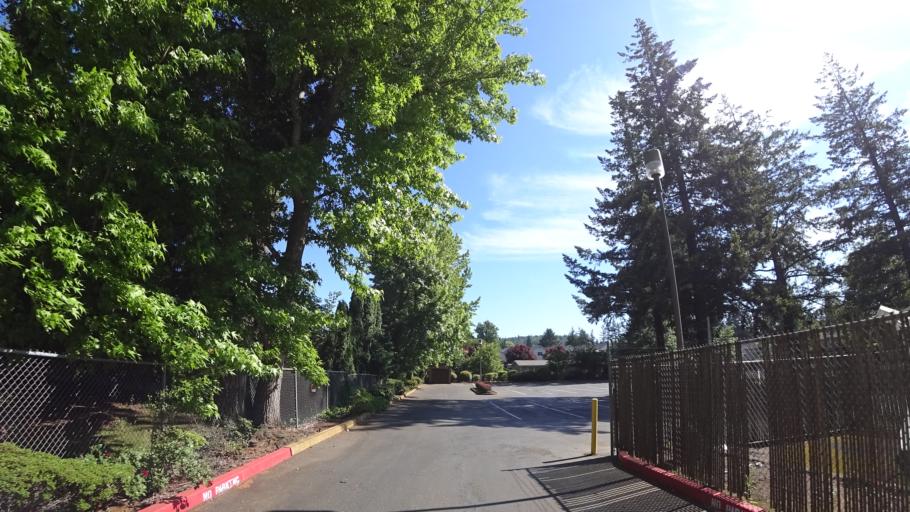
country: US
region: Oregon
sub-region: Multnomah County
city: Gresham
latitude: 45.4960
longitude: -122.4744
